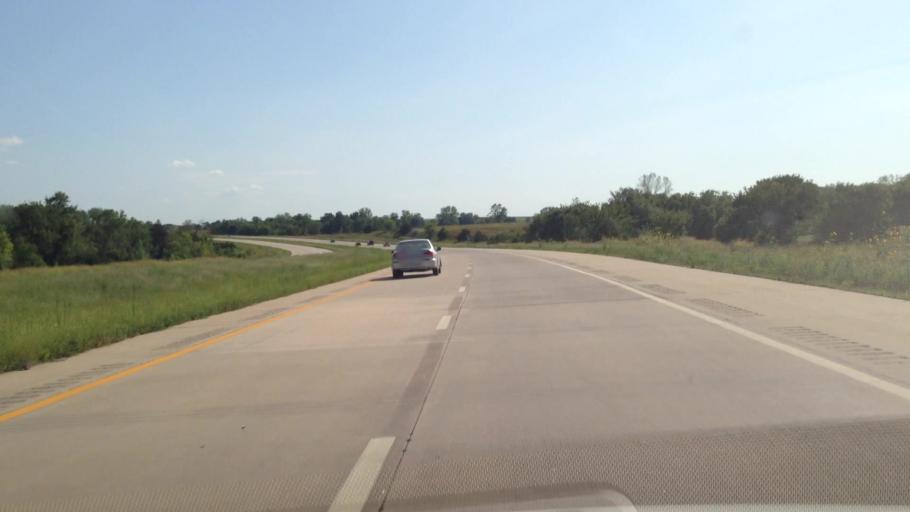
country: US
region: Kansas
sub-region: Bourbon County
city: Fort Scott
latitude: 37.9660
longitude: -94.7075
